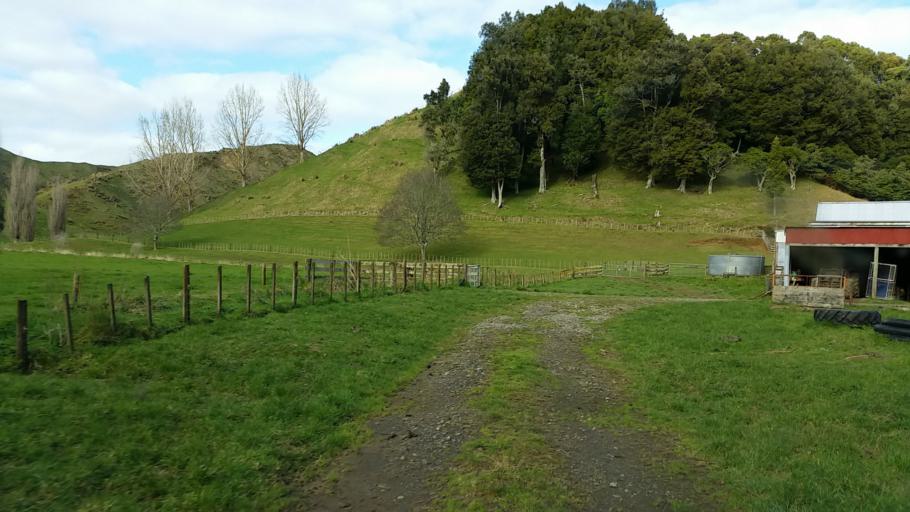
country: NZ
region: Taranaki
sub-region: South Taranaki District
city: Eltham
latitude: -39.2514
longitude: 174.5426
